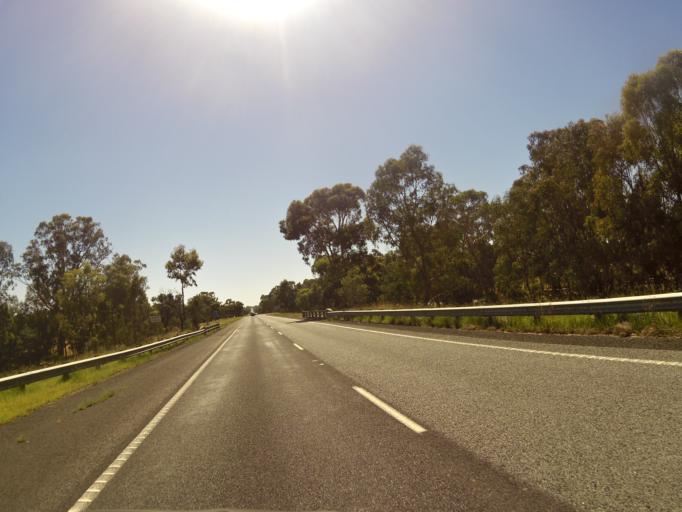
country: AU
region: Victoria
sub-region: Greater Shepparton
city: Shepparton
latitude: -36.8505
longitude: 145.3357
